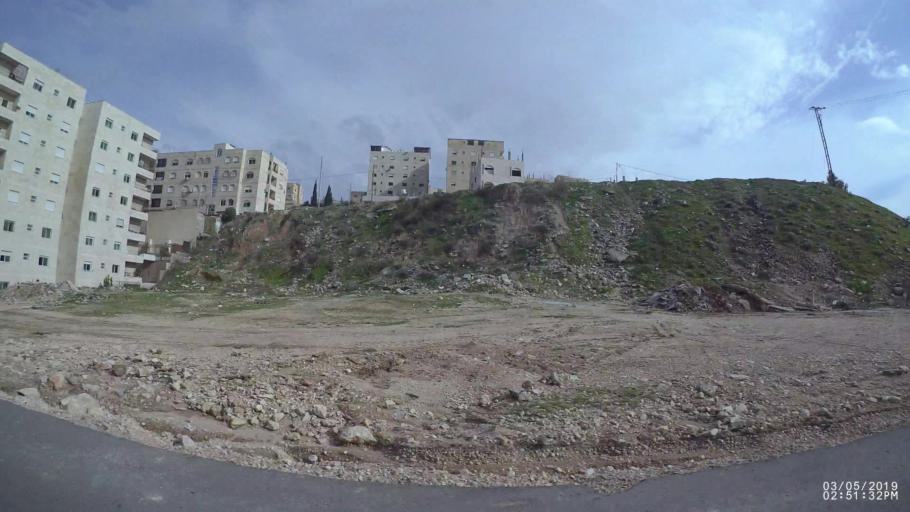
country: JO
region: Amman
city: Amman
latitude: 32.0112
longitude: 35.9472
